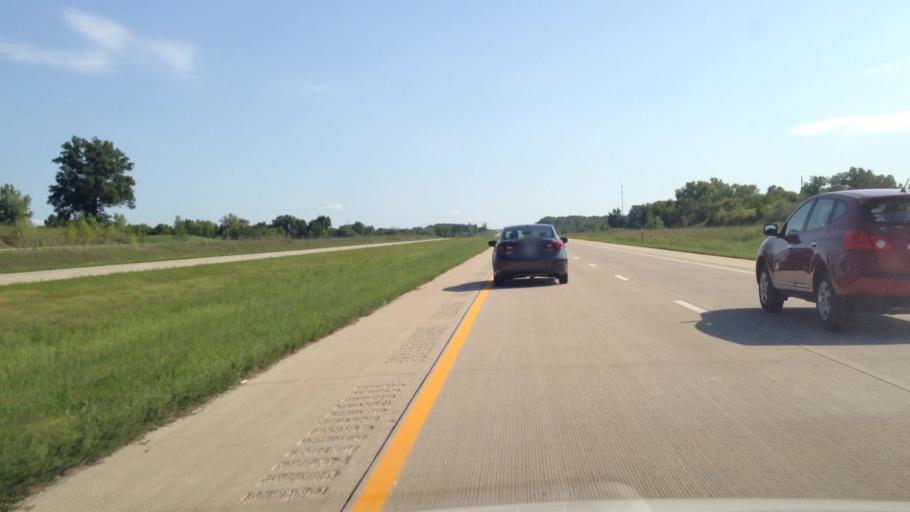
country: US
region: Kansas
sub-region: Linn County
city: Pleasanton
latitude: 38.1304
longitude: -94.7120
